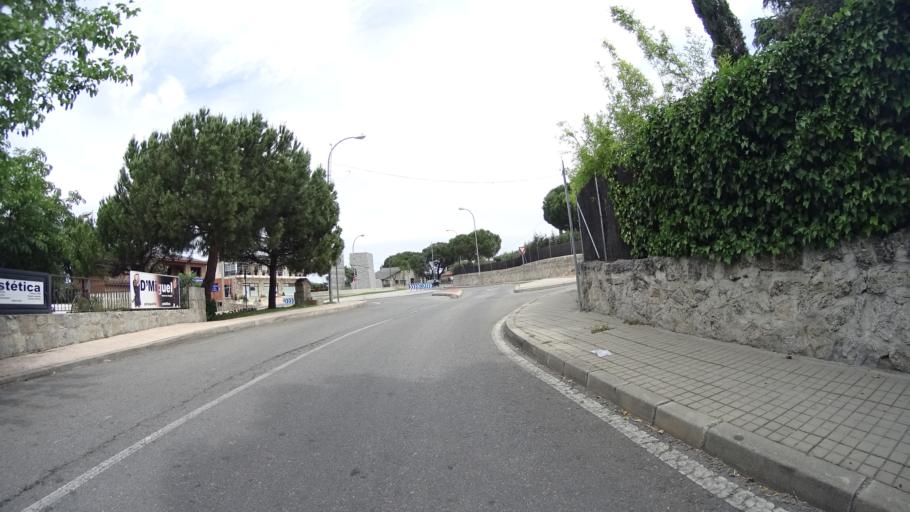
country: ES
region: Madrid
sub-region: Provincia de Madrid
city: Colmenarejo
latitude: 40.5653
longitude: -4.0135
